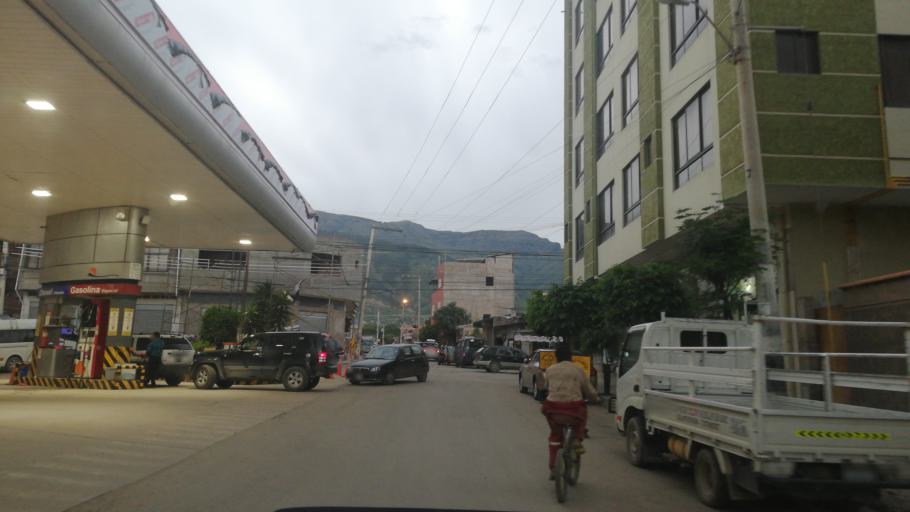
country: BO
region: Cochabamba
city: Cochabamba
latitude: -17.3386
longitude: -66.2225
